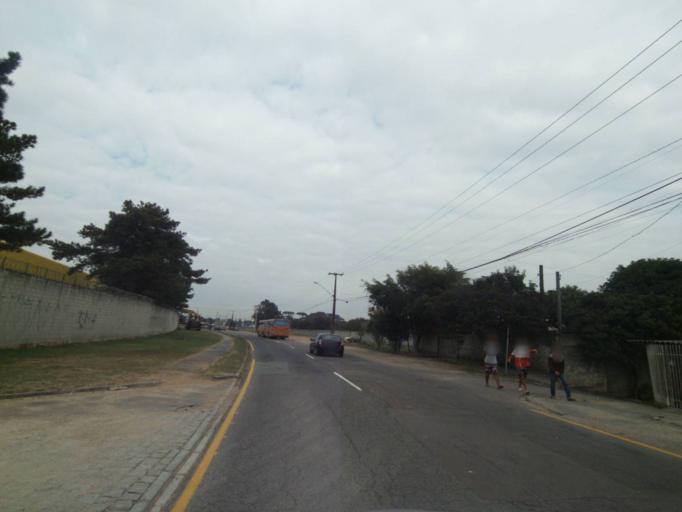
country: BR
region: Parana
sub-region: Curitiba
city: Curitiba
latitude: -25.5177
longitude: -49.3269
